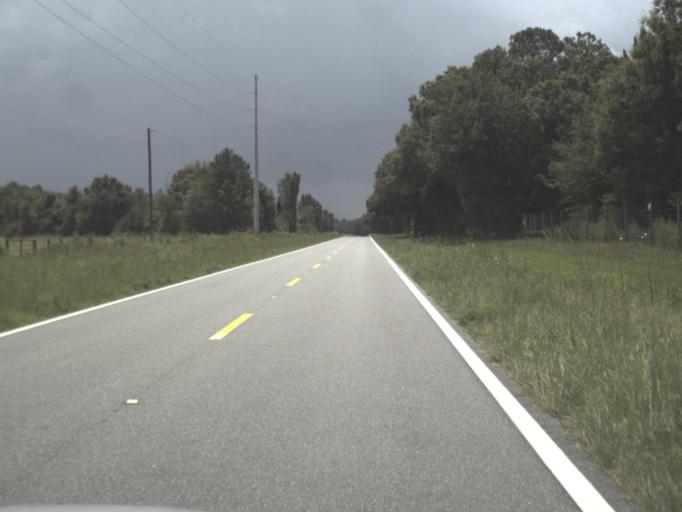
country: US
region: Florida
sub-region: Union County
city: Lake Butler
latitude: 29.8995
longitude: -82.3596
